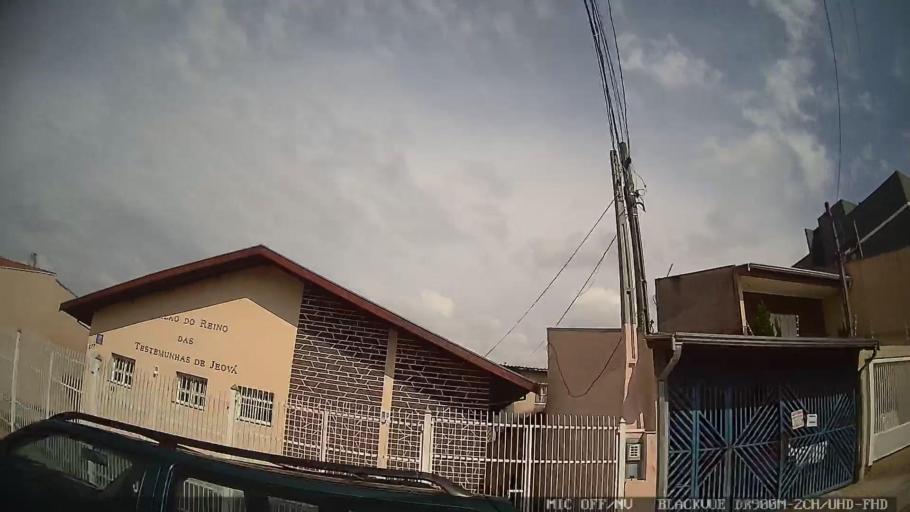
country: BR
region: Sao Paulo
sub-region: Indaiatuba
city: Indaiatuba
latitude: -23.1281
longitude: -47.2402
